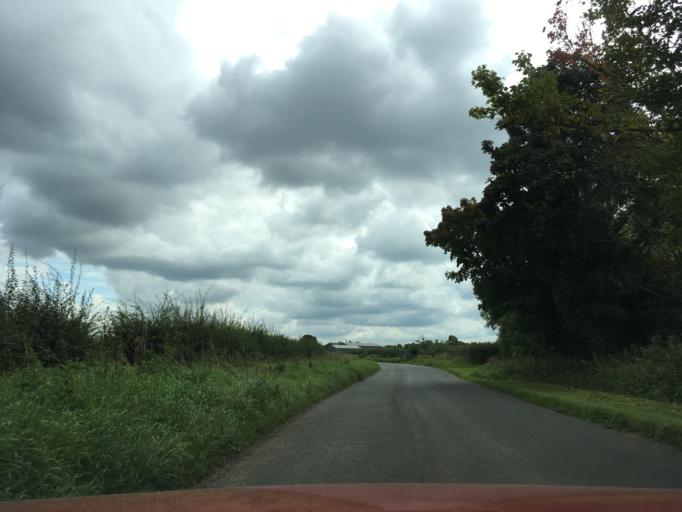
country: GB
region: England
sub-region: Gloucestershire
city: Berkeley
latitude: 51.6778
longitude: -2.4261
